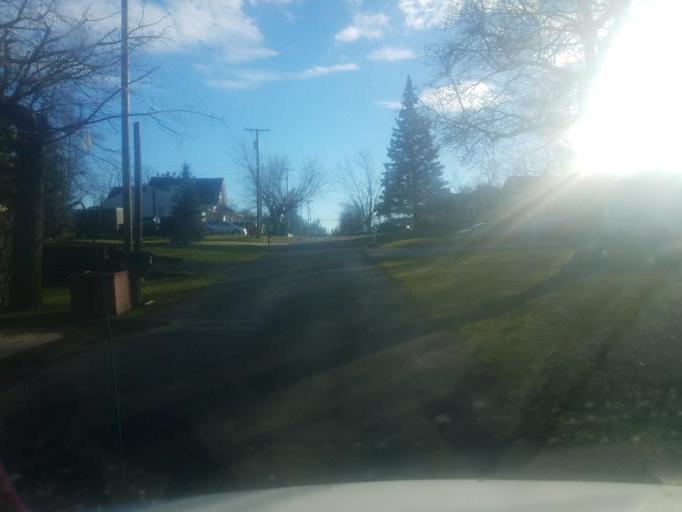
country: US
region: Ohio
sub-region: Richland County
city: Mansfield
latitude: 40.7889
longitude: -82.5485
